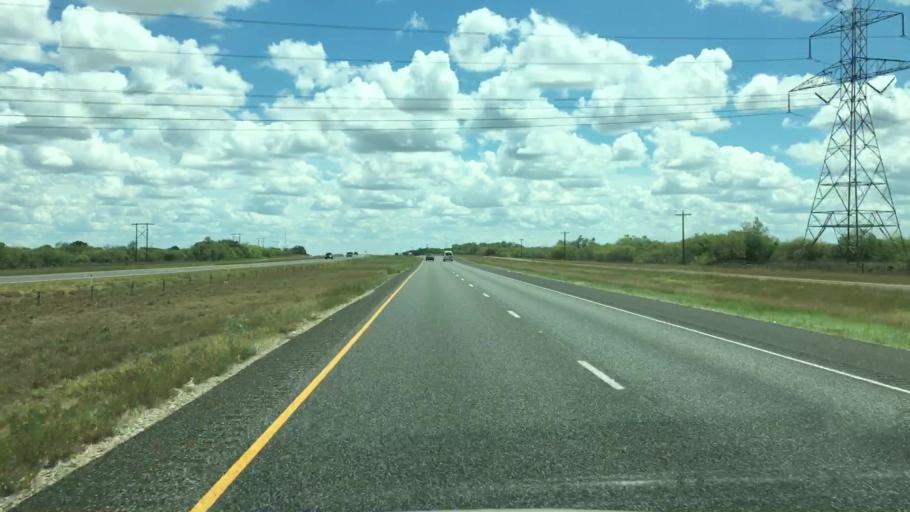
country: US
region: Texas
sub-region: Atascosa County
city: Pleasanton
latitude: 28.8223
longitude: -98.3629
